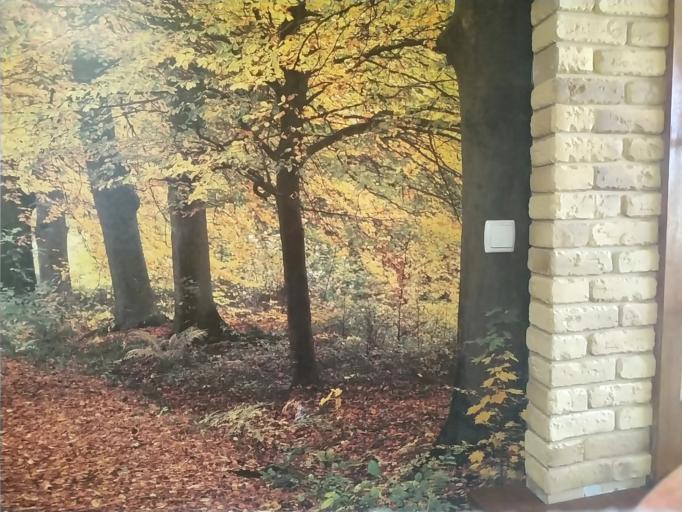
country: RU
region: Tverskaya
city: Krasnomayskiy
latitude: 57.7050
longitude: 34.4903
